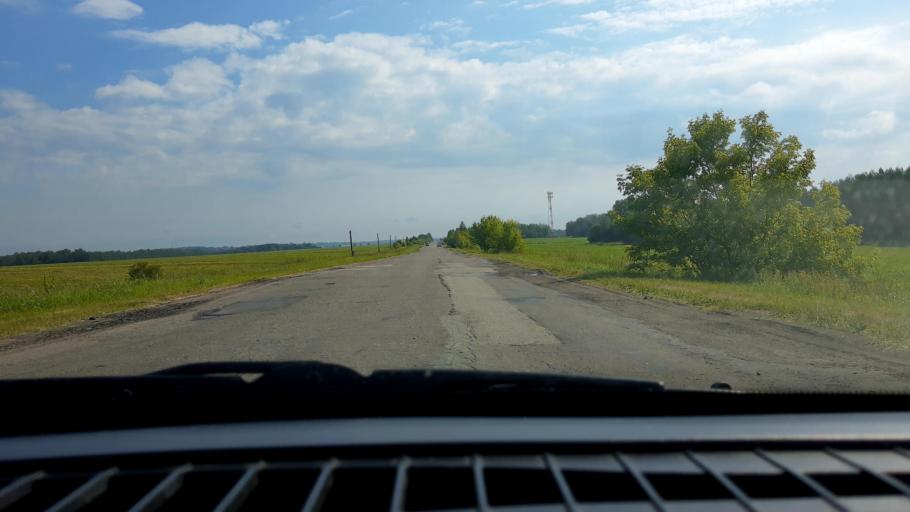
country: RU
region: Nizjnij Novgorod
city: Kstovo
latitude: 56.1132
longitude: 44.3001
